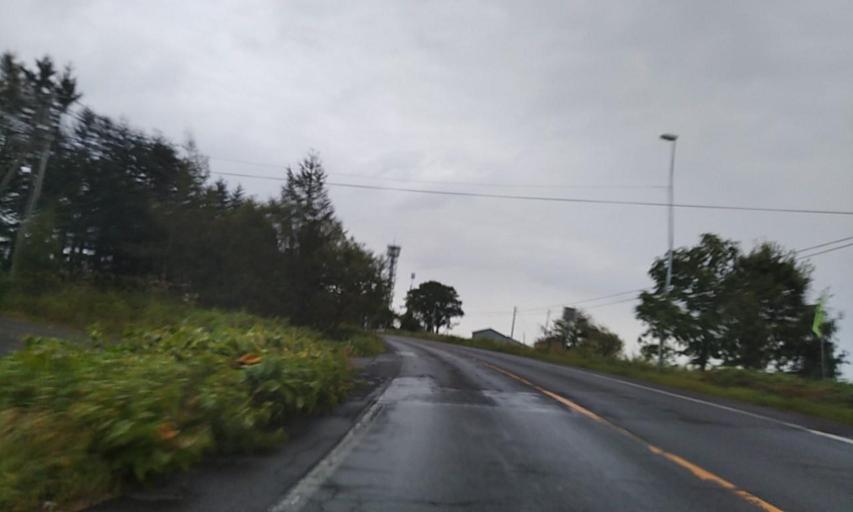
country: JP
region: Hokkaido
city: Mombetsu
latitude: 44.4828
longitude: 143.0970
